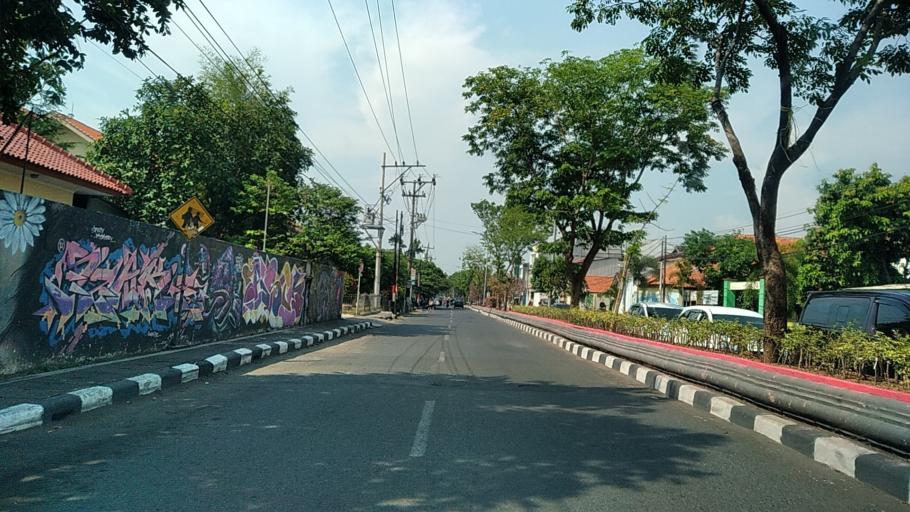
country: ID
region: Central Java
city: Semarang
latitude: -7.0056
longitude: 110.4544
